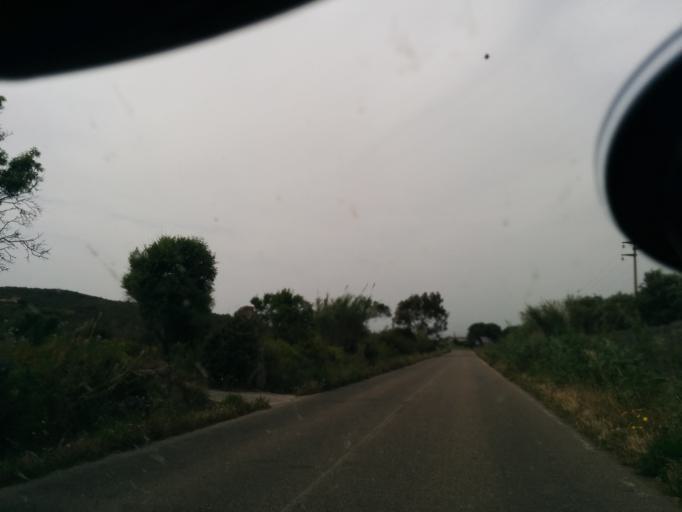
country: IT
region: Sardinia
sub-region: Provincia di Carbonia-Iglesias
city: Sant'Antioco
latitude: 39.0383
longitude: 8.4543
